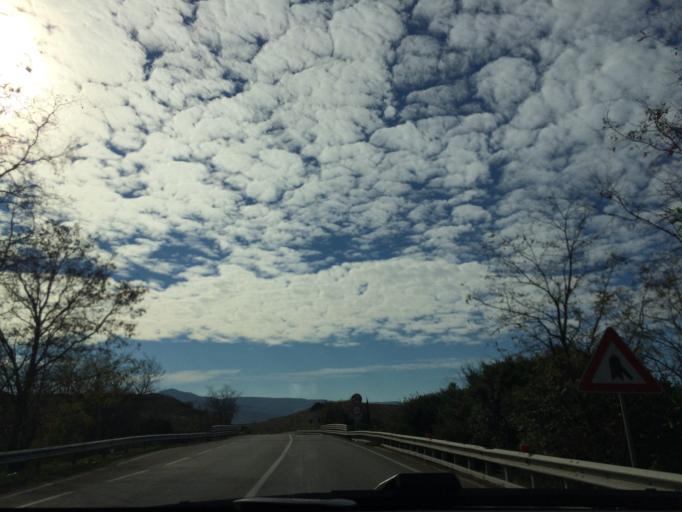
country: IT
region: Basilicate
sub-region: Provincia di Matera
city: La Martella
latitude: 40.6041
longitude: 16.5677
